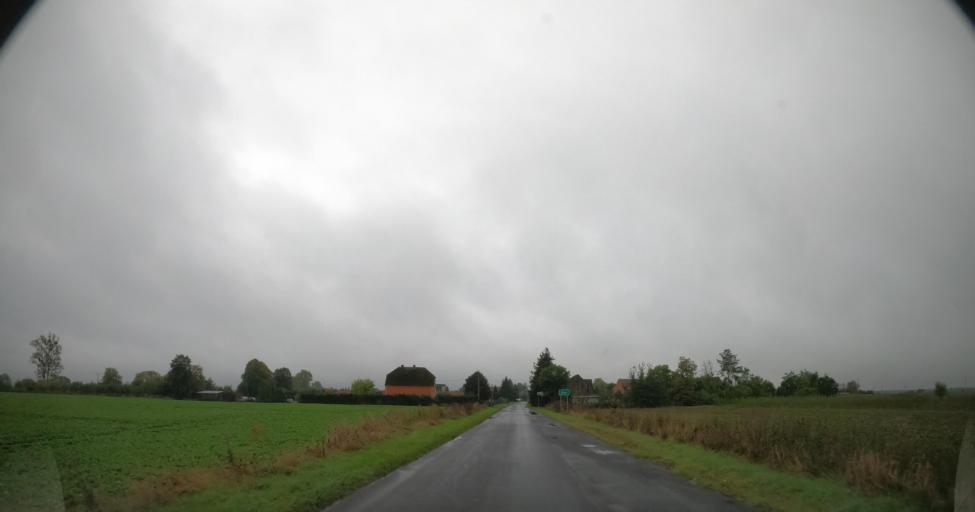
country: PL
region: West Pomeranian Voivodeship
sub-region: Powiat pyrzycki
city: Kozielice
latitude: 53.0518
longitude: 14.7756
